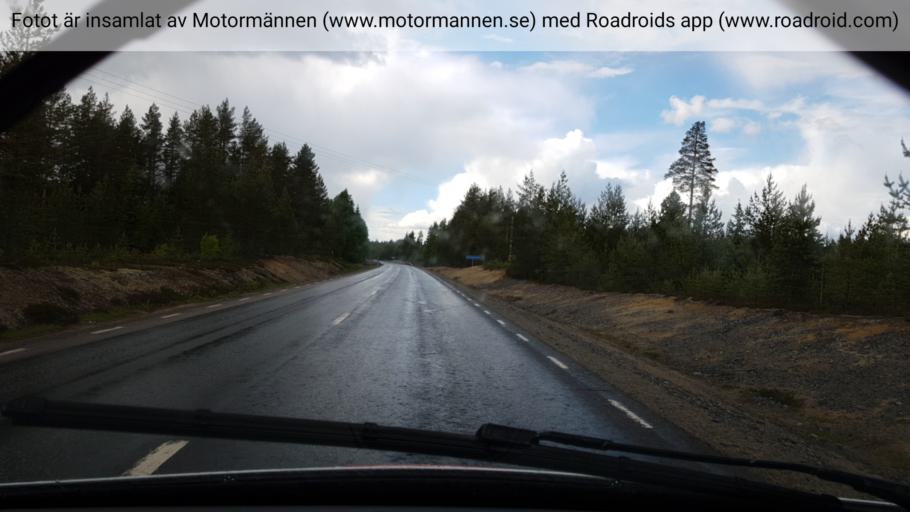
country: SE
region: Vaesterbotten
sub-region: Umea Kommun
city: Roback
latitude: 63.9673
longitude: 20.1215
